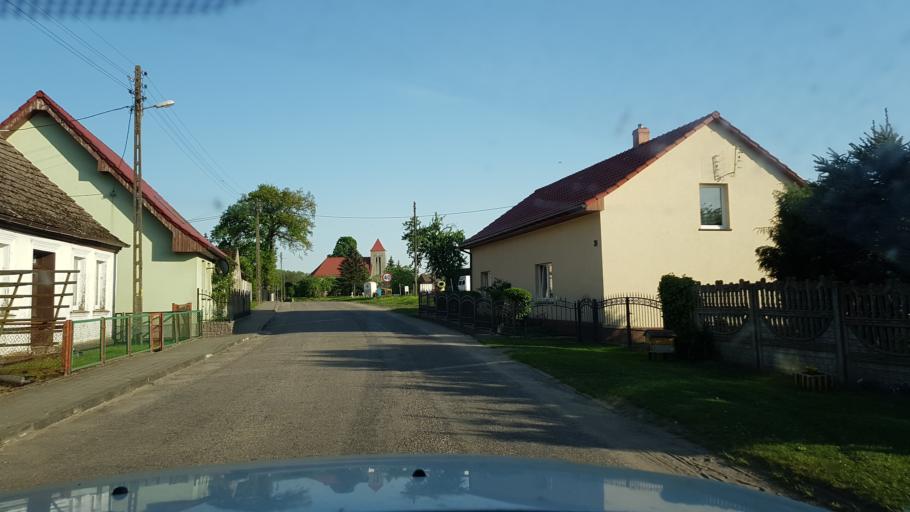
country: PL
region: West Pomeranian Voivodeship
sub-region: Powiat lobeski
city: Dobra
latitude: 53.6336
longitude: 15.3595
